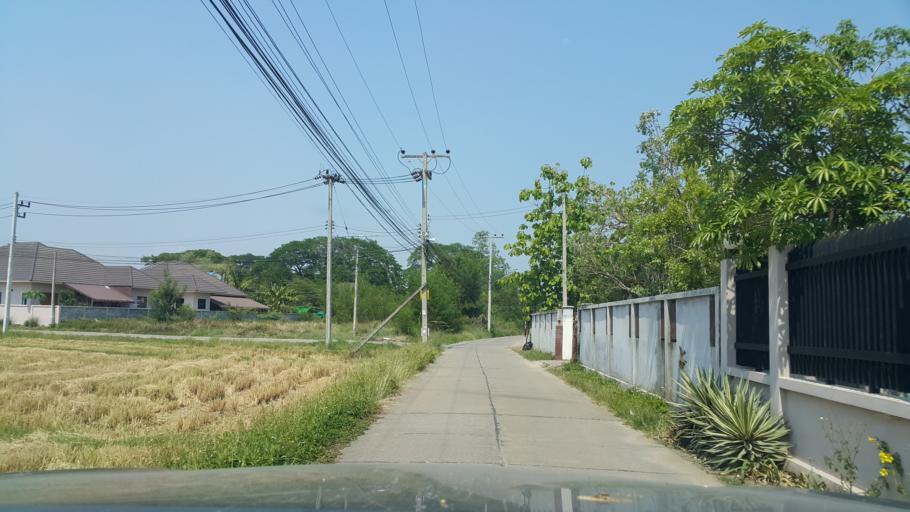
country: TH
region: Chiang Mai
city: Saraphi
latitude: 18.7250
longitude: 98.9724
